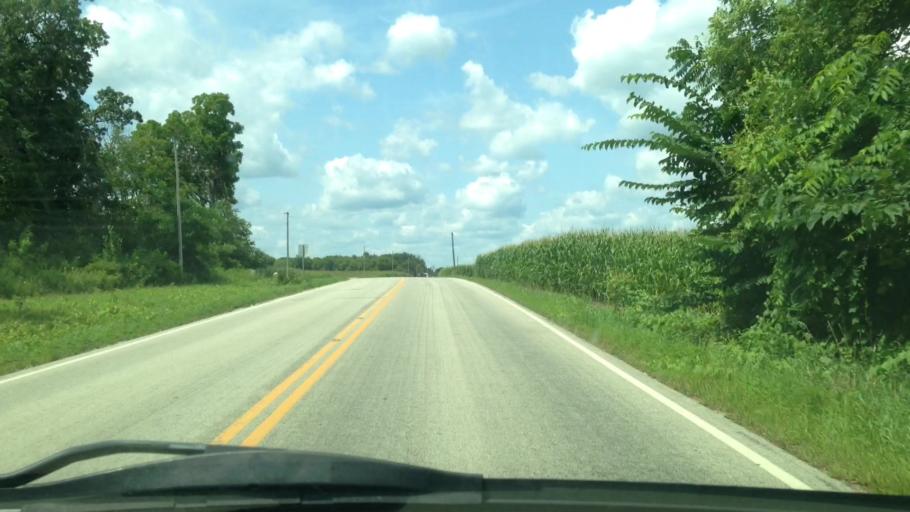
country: US
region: Minnesota
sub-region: Olmsted County
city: Rochester
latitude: 43.9533
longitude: -92.5070
